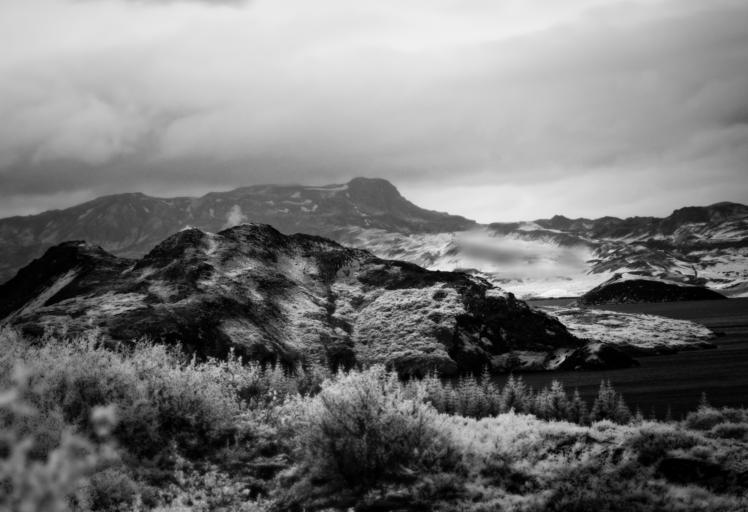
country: IS
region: South
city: Hveragerdi
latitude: 64.2489
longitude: -21.0230
